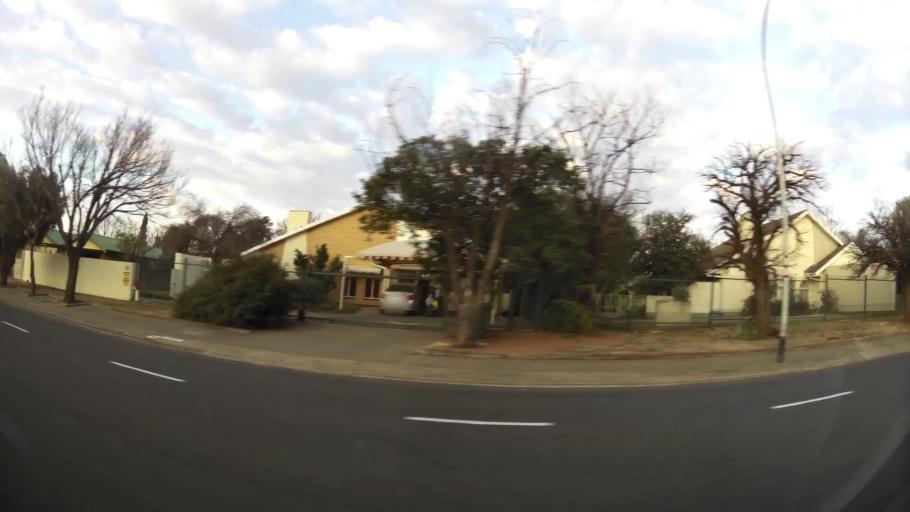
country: ZA
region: Orange Free State
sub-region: Mangaung Metropolitan Municipality
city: Bloemfontein
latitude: -29.1416
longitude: 26.1755
